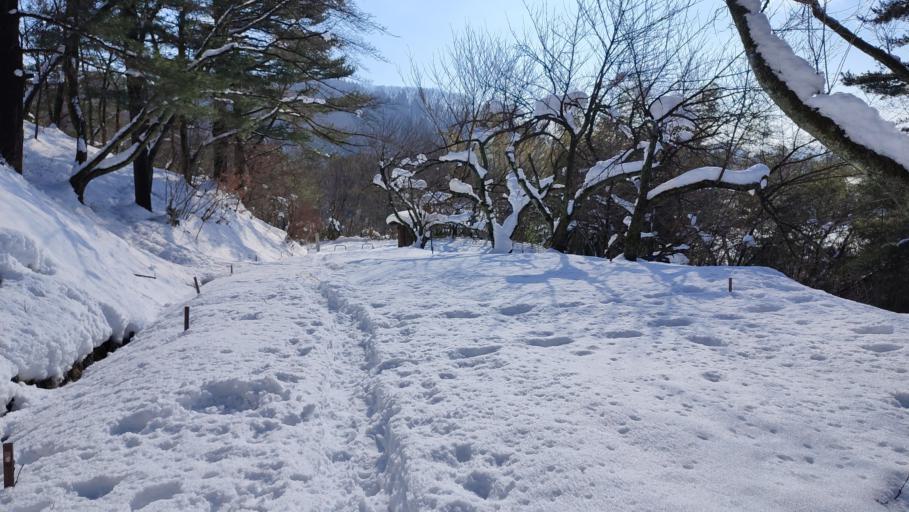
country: JP
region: Akita
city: Kakunodatemachi
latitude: 39.6045
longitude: 140.5622
